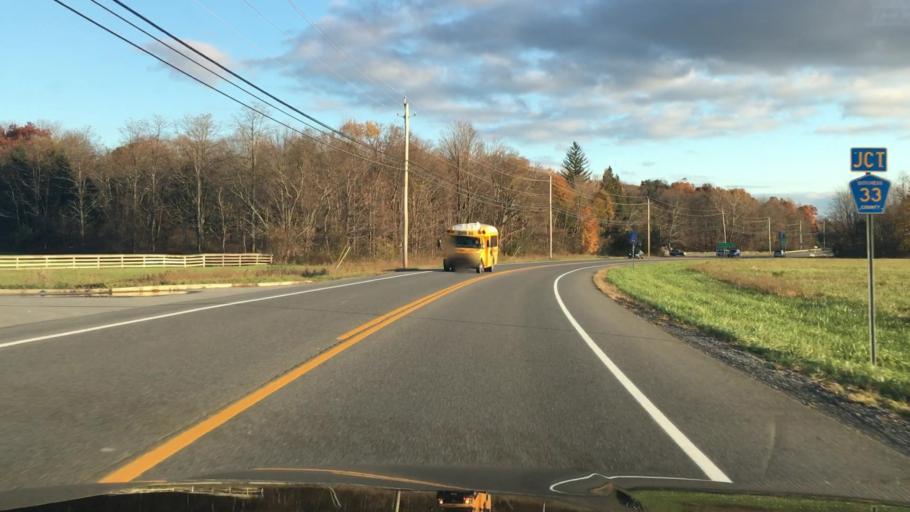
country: US
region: New York
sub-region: Dutchess County
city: Hillside Lake
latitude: 41.6437
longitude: -73.7956
